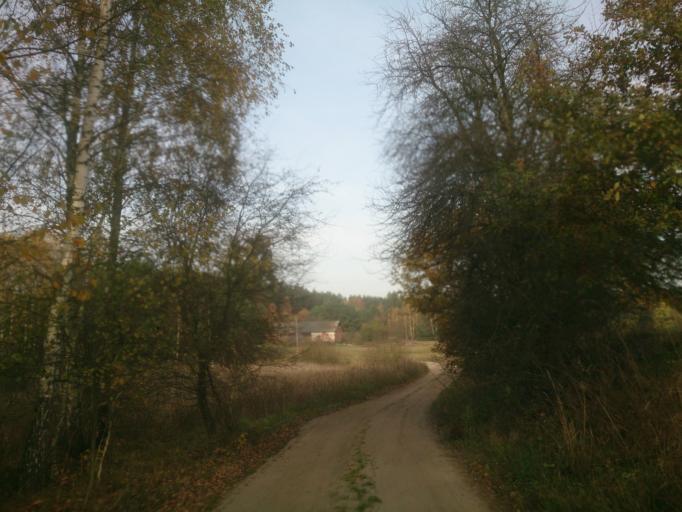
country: PL
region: Kujawsko-Pomorskie
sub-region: Powiat brodnicki
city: Bobrowo
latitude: 53.3718
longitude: 19.3437
